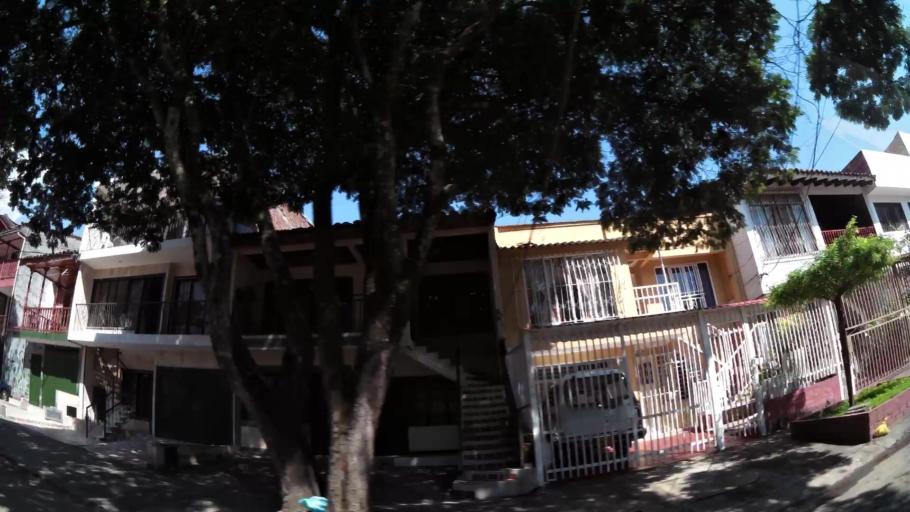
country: CO
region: Valle del Cauca
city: Cali
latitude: 3.4303
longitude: -76.5284
